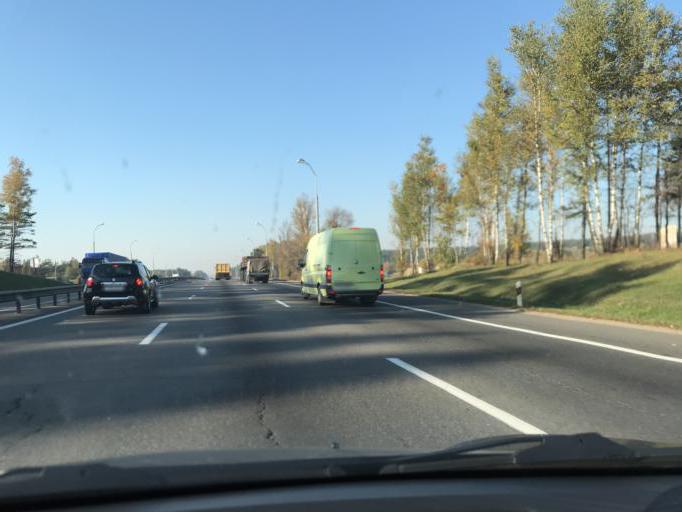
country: BY
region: Minsk
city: Pryvol'ny
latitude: 53.8184
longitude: 27.7670
